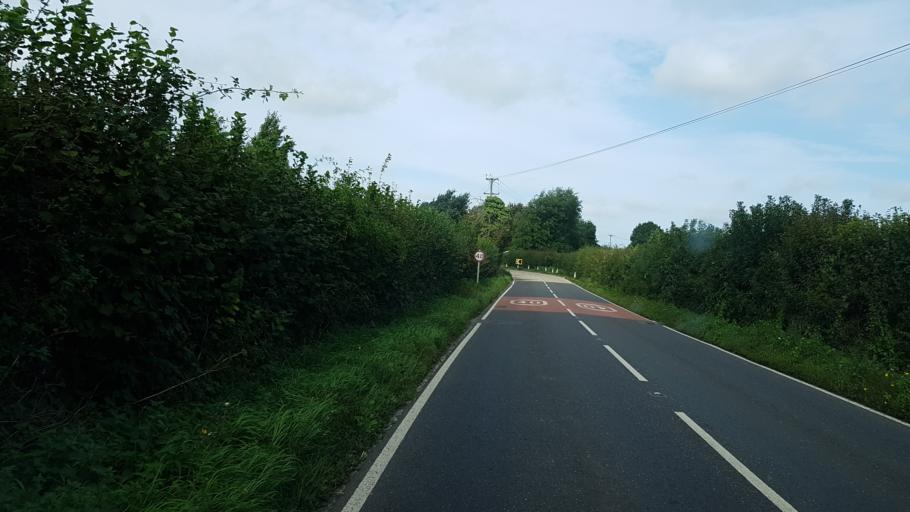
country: GB
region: England
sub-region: Kent
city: Maidstone
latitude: 51.2275
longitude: 0.5556
